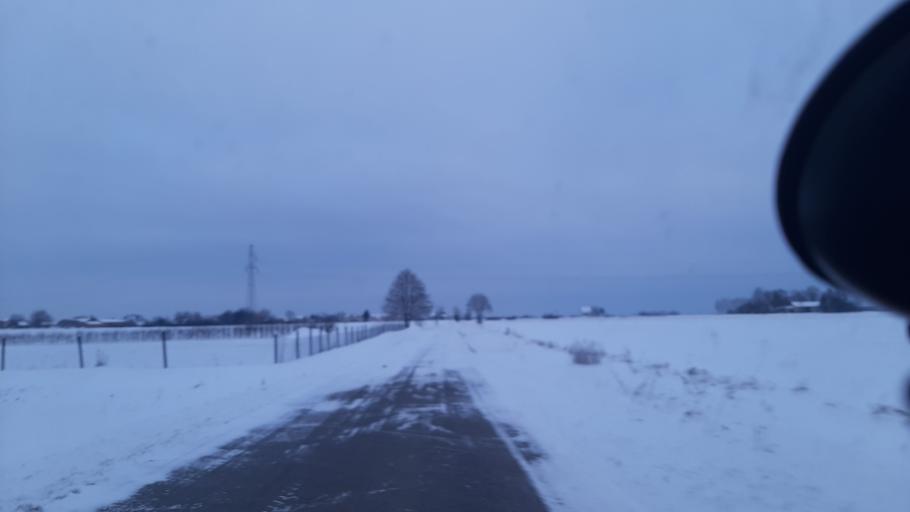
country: PL
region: Lublin Voivodeship
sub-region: Powiat lubelski
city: Jastkow
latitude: 51.3488
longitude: 22.4079
